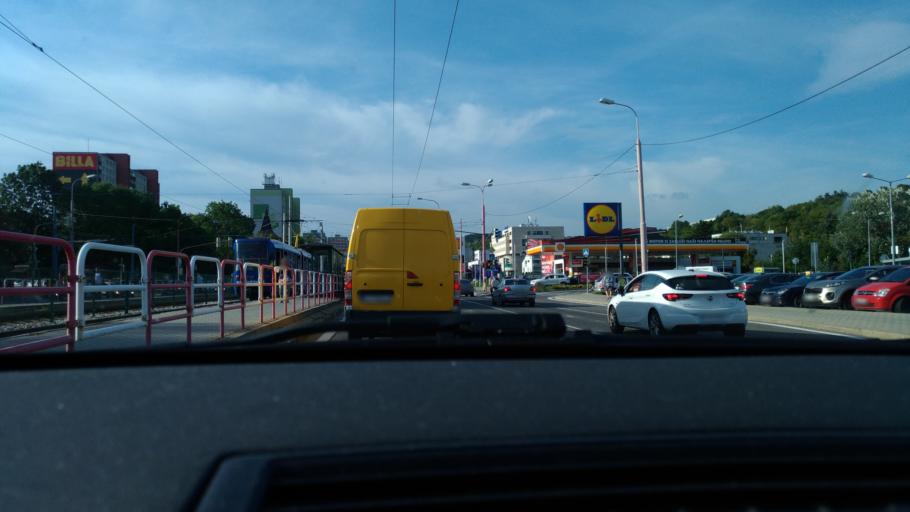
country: SK
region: Bratislavsky
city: Bratislava
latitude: 48.1494
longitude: 17.0633
